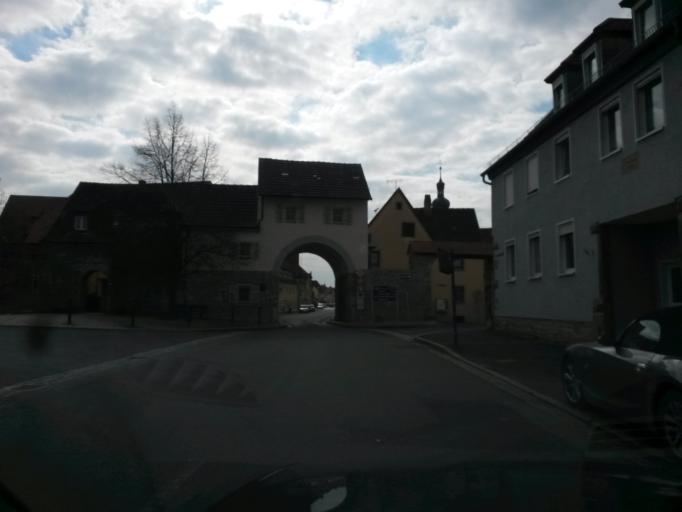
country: DE
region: Bavaria
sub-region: Regierungsbezirk Unterfranken
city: Eibelstadt
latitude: 49.7261
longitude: 9.9986
